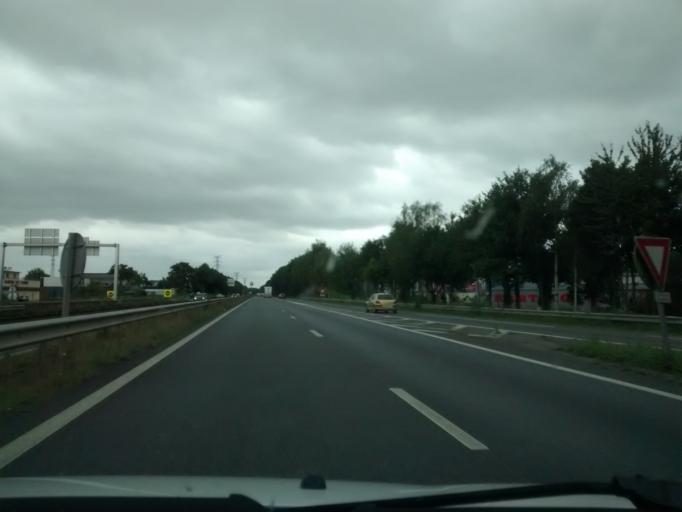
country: FR
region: Brittany
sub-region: Departement d'Ille-et-Vilaine
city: La Chapelle-des-Fougeretz
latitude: 48.2031
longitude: -1.7332
